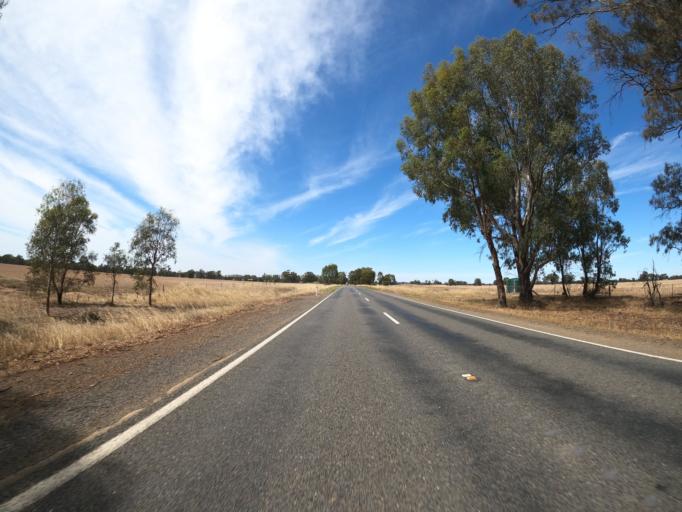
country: AU
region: Victoria
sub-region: Benalla
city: Benalla
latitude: -36.2852
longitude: 145.9523
